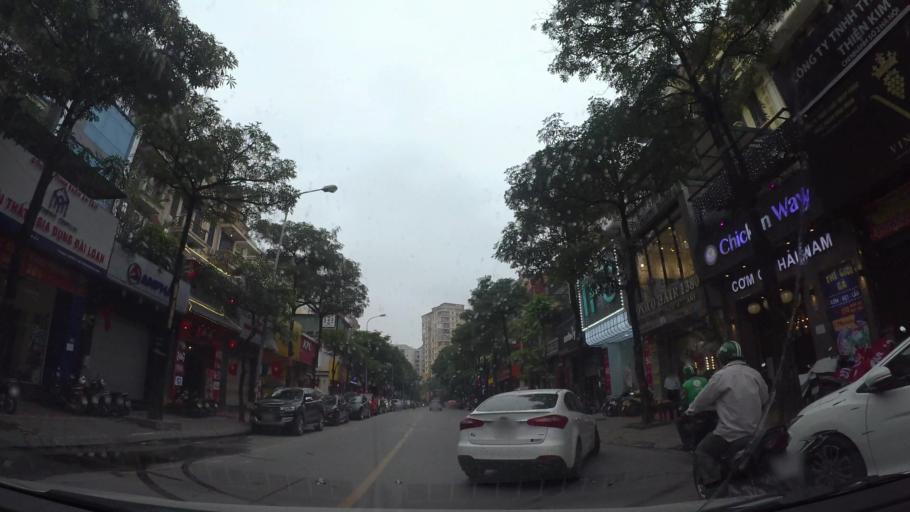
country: VN
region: Ha Noi
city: Cau Giay
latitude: 21.0160
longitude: 105.8004
